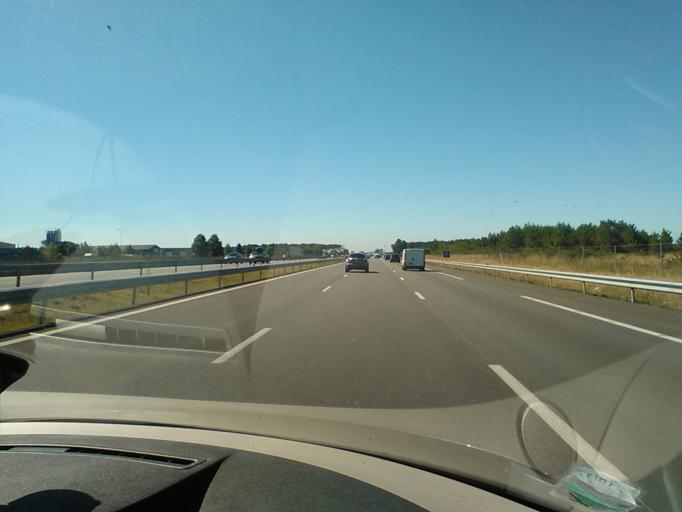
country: FR
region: Aquitaine
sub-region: Departement des Landes
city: Saint-Geours-de-Maremne
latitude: 43.7217
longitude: -1.2276
